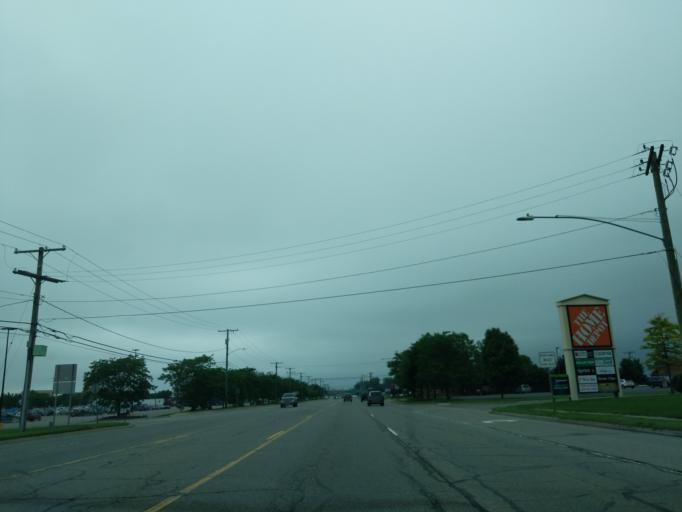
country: US
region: Michigan
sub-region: Branch County
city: Coldwater
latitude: 41.9349
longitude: -84.9655
